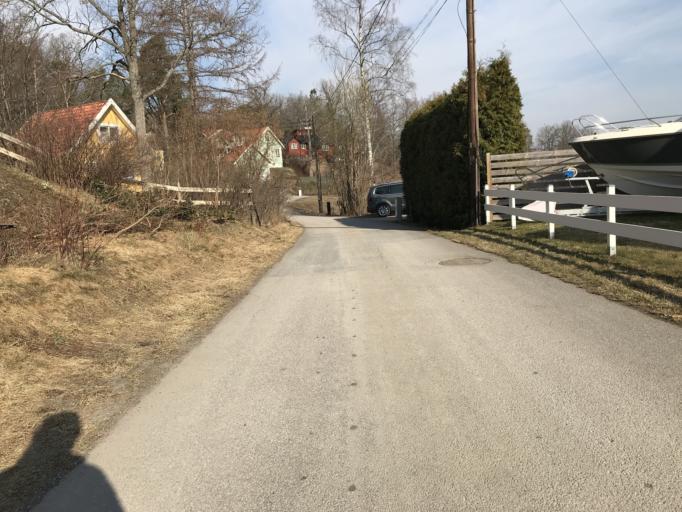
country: SE
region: Stockholm
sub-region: Osterakers Kommun
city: Akersberga
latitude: 59.4730
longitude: 18.3060
